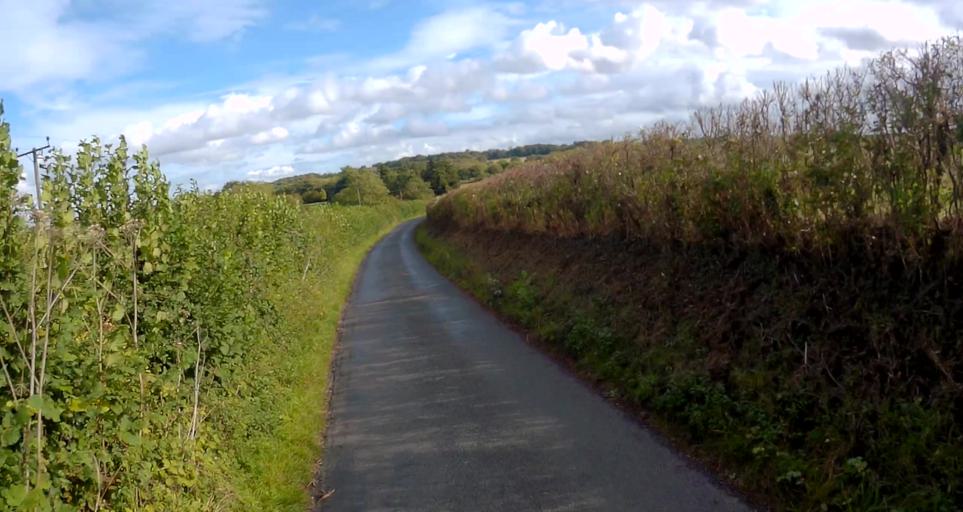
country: GB
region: England
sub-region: Hampshire
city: Kings Worthy
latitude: 51.0840
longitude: -1.2133
